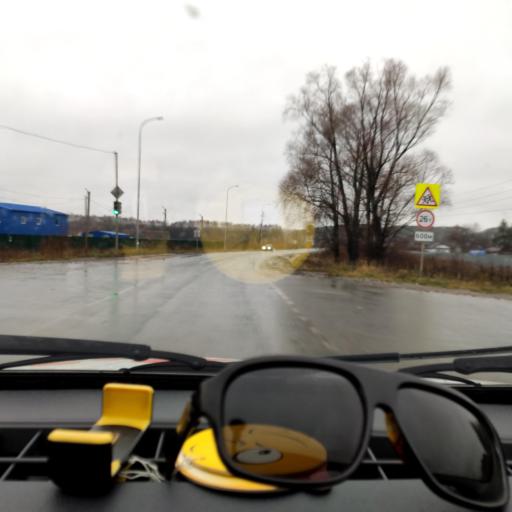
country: RU
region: Bashkortostan
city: Iglino
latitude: 54.8291
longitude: 56.3916
